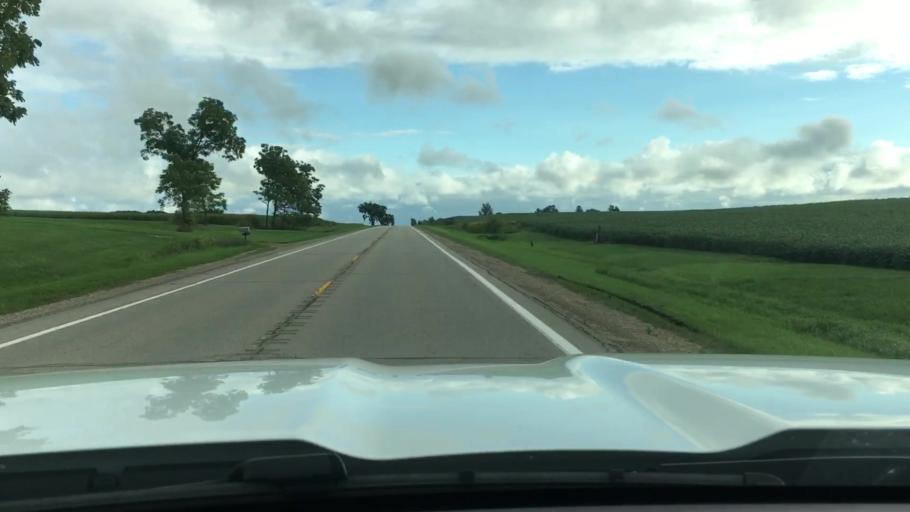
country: US
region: Michigan
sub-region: Tuscola County
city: Caro
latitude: 43.5640
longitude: -83.3088
